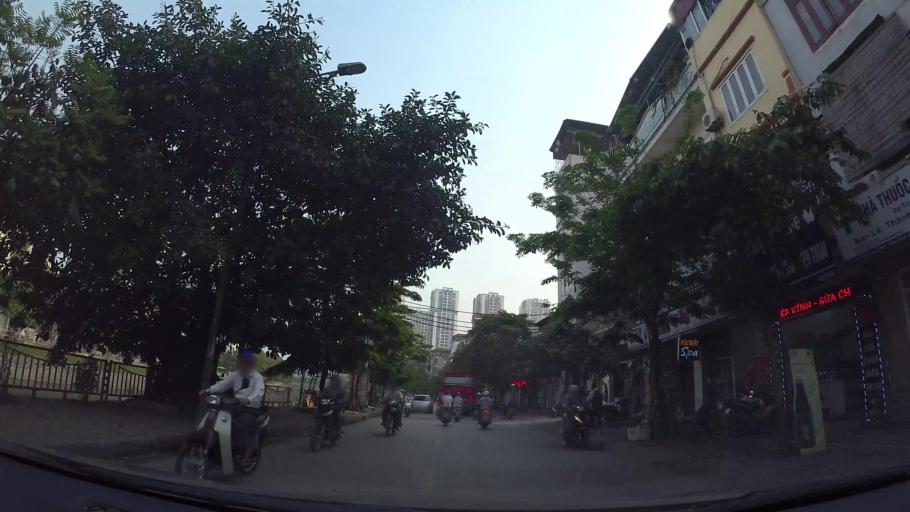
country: VN
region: Ha Noi
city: Thanh Xuan
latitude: 20.9895
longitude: 105.8130
